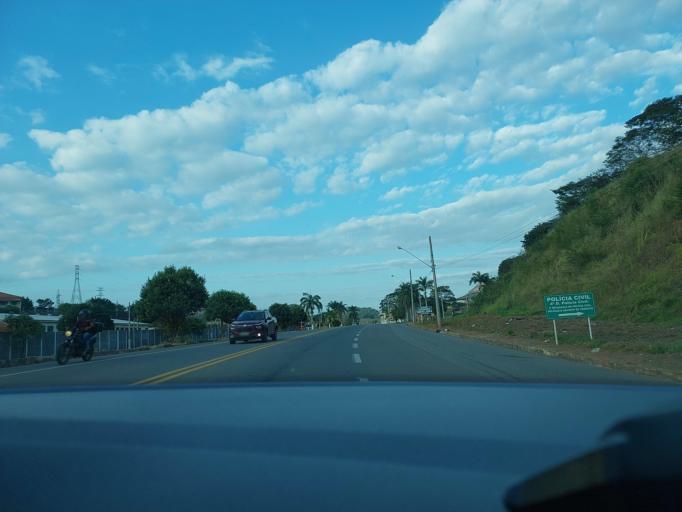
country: BR
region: Minas Gerais
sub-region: Muriae
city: Muriae
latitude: -21.1270
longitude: -42.3436
